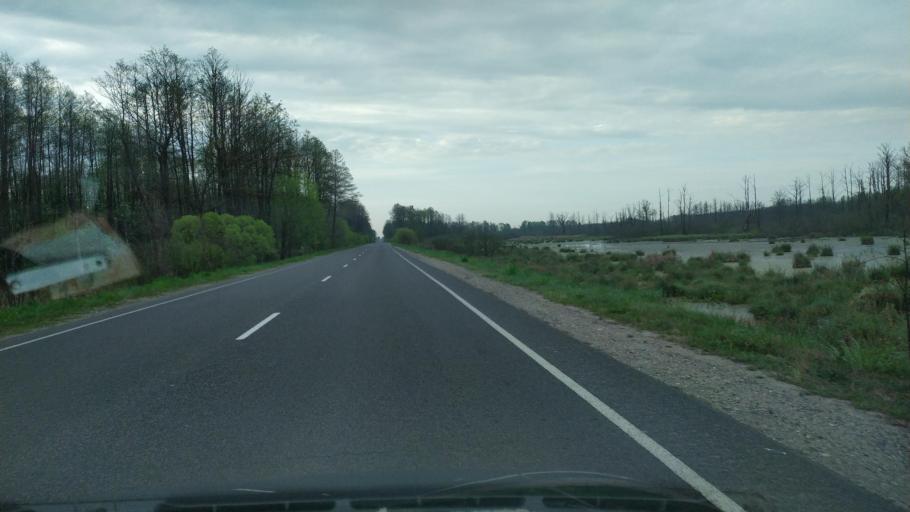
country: BY
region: Brest
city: Zhabinka
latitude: 52.2746
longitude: 23.9528
